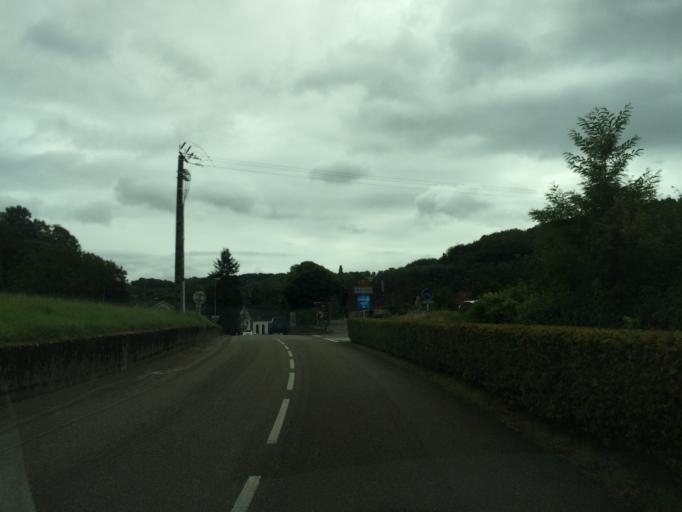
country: FR
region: Alsace
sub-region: Departement du Bas-Rhin
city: Wissembourg
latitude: 49.0403
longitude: 7.9036
